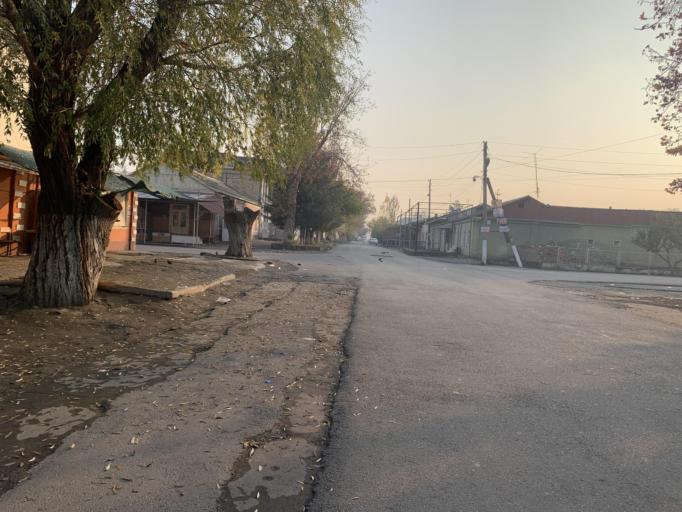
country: UZ
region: Fergana
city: Qo`qon
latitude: 40.5228
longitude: 70.9382
